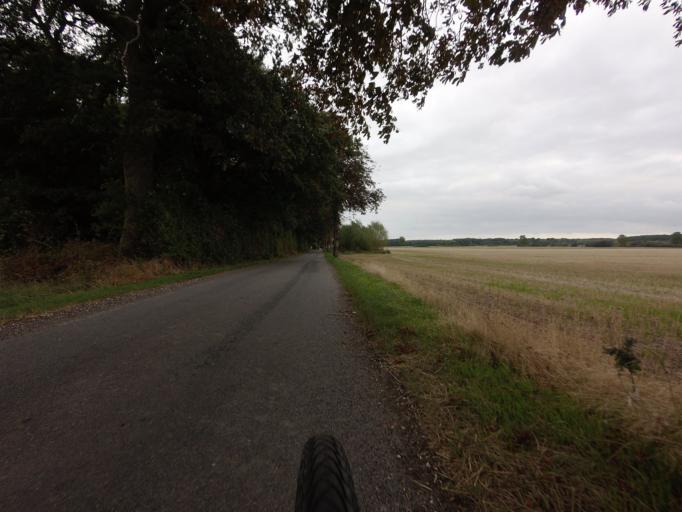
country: DK
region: Zealand
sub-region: Stevns Kommune
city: Store Heddinge
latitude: 55.3297
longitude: 12.3306
